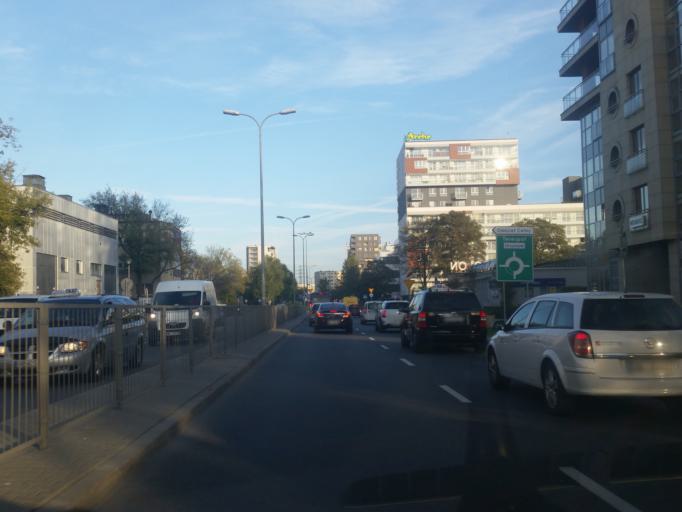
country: PL
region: Masovian Voivodeship
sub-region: Warszawa
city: Mokotow
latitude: 52.1765
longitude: 20.9934
